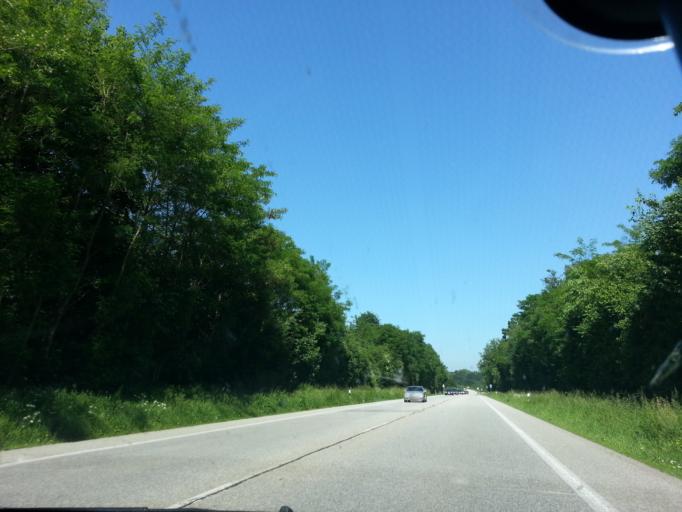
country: DE
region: Schleswig-Holstein
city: Alt Molln
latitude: 53.6149
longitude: 10.6503
